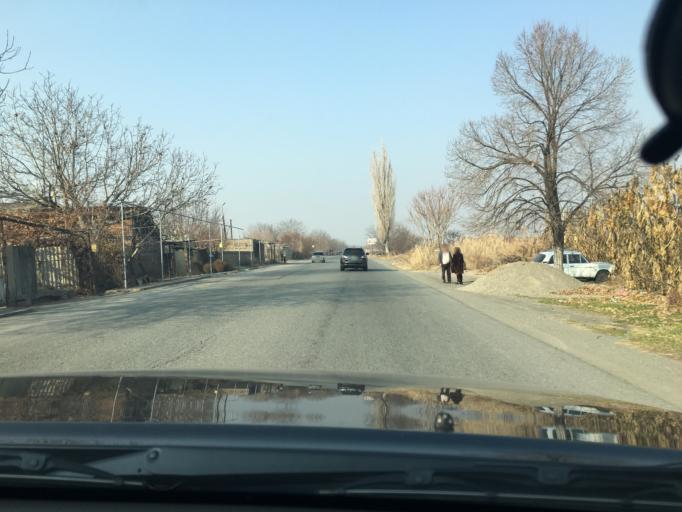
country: AM
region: Armavir
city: Myasnikyan
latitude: 40.1738
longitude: 43.9542
